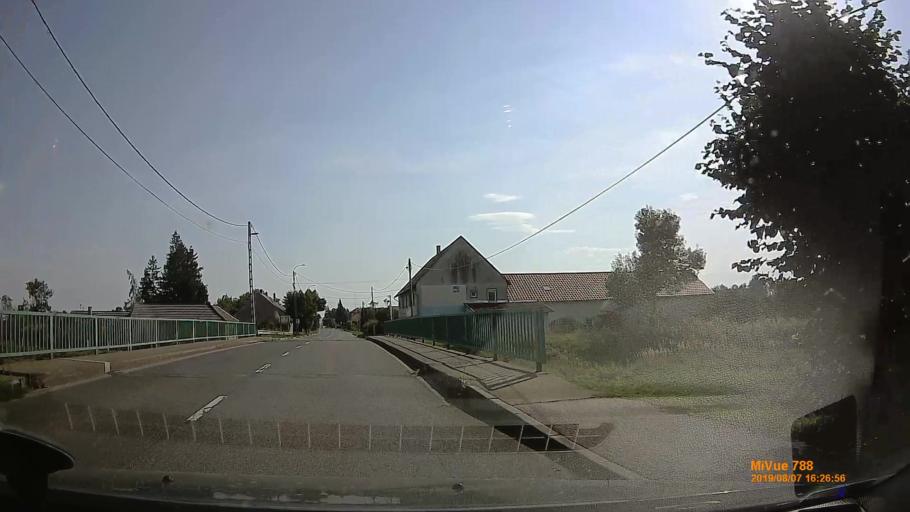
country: HU
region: Zala
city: Lenti
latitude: 46.7057
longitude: 16.5515
